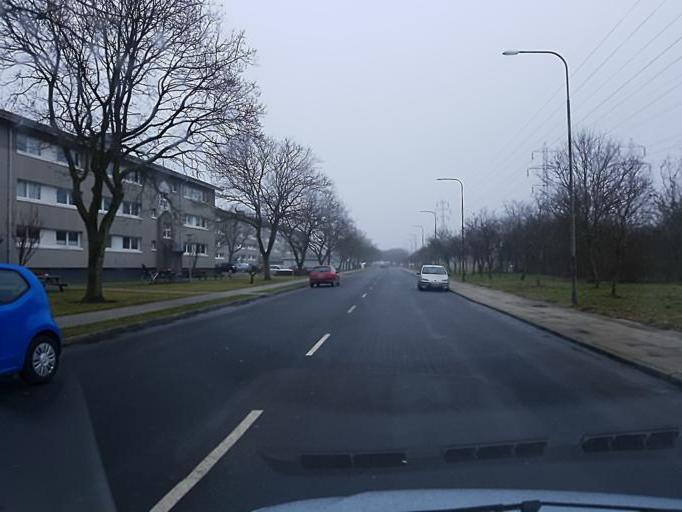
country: DK
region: South Denmark
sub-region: Esbjerg Kommune
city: Esbjerg
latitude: 55.4770
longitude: 8.5003
